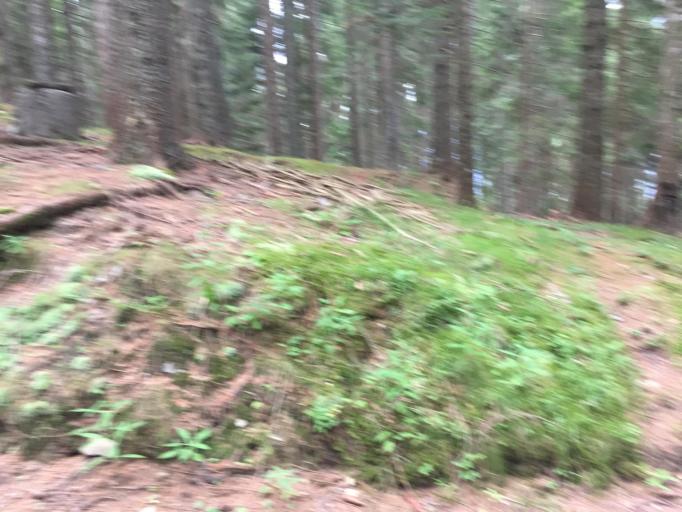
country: IT
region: Friuli Venezia Giulia
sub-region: Provincia di Udine
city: Forni Avoltri
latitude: 46.5864
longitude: 12.8096
